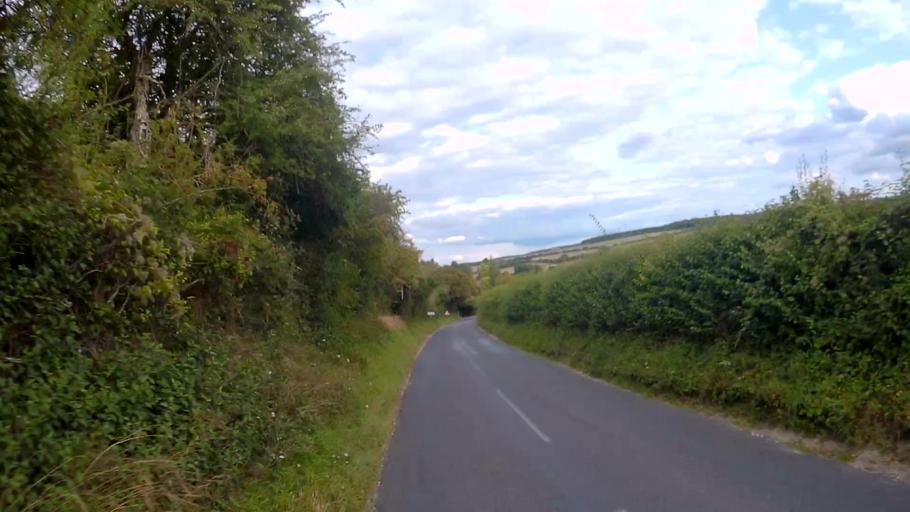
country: GB
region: England
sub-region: Hampshire
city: Kings Worthy
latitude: 51.1381
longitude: -1.1908
